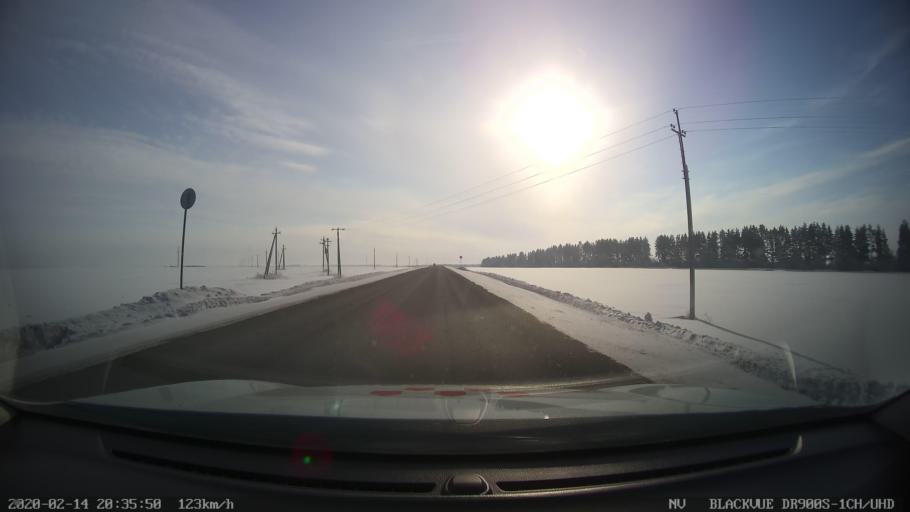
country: RU
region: Tatarstan
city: Kuybyshevskiy Zaton
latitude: 55.3768
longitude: 48.9912
